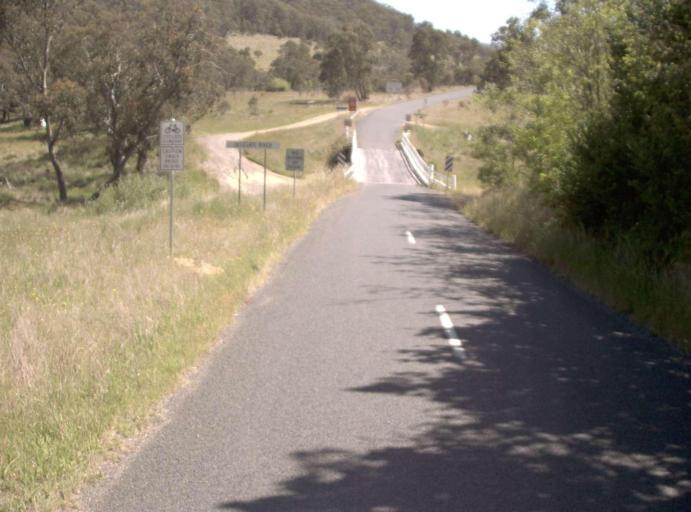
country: AU
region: New South Wales
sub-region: Bombala
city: Bombala
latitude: -37.0463
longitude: 148.8130
